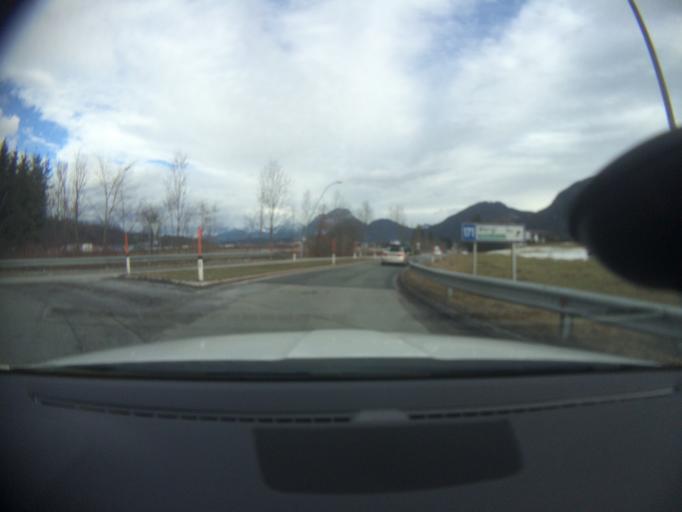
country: AT
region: Tyrol
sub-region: Politischer Bezirk Kufstein
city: Worgl
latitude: 47.4784
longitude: 12.0316
